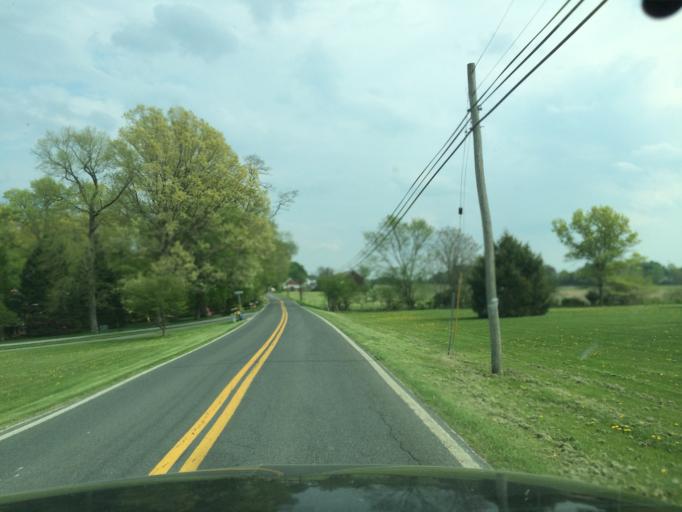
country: US
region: Maryland
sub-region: Carroll County
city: Eldersburg
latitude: 39.4419
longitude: -77.0234
